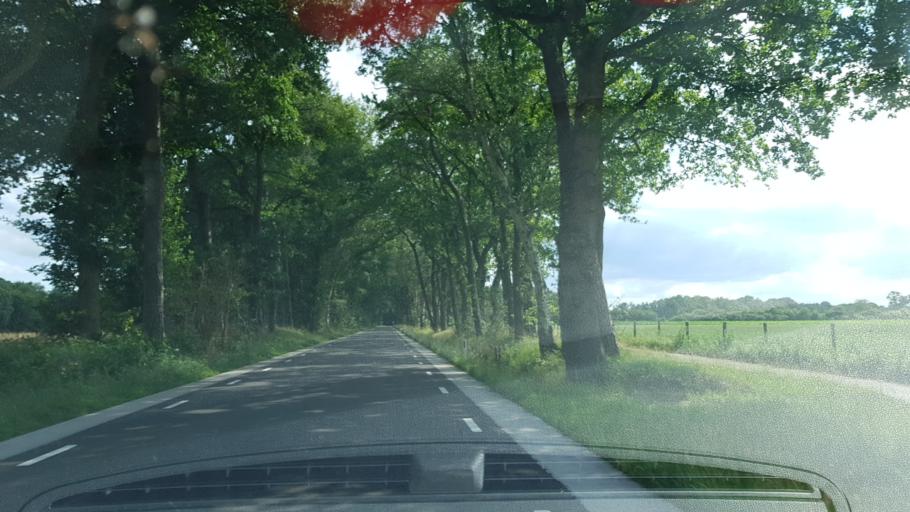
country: NL
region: Gelderland
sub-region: Gemeente Barneveld
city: Garderen
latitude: 52.2784
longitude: 5.7306
